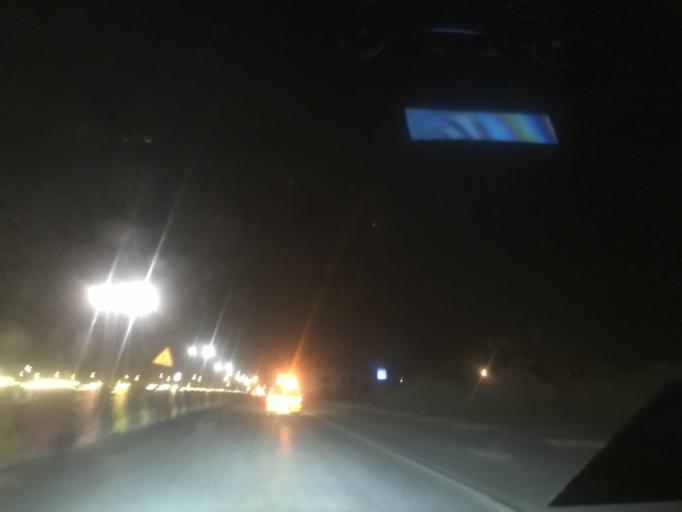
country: SA
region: Ar Riyad
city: Riyadh
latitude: 24.7977
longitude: 46.5925
